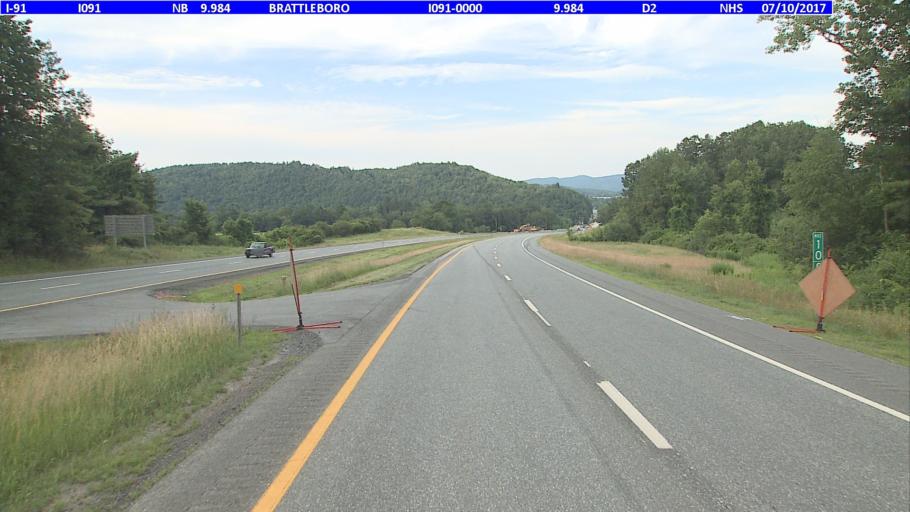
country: US
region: Vermont
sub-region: Windham County
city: Brattleboro
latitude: 42.8681
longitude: -72.5777
